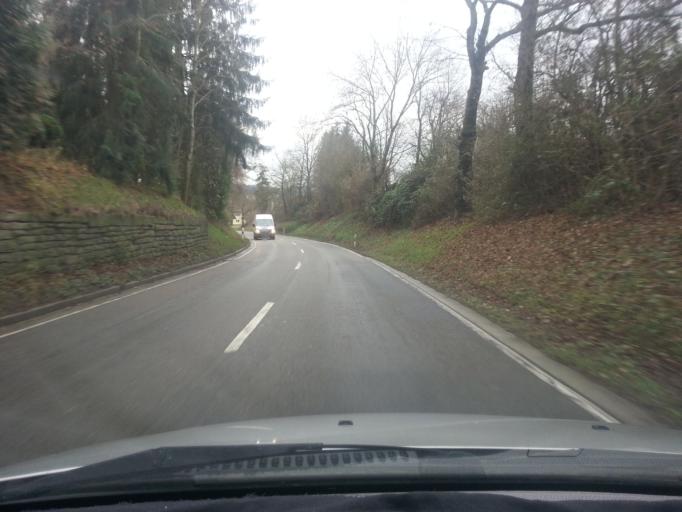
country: DE
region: Baden-Wuerttemberg
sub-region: Regierungsbezirk Stuttgart
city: Ittlingen
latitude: 49.1744
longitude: 8.9383
